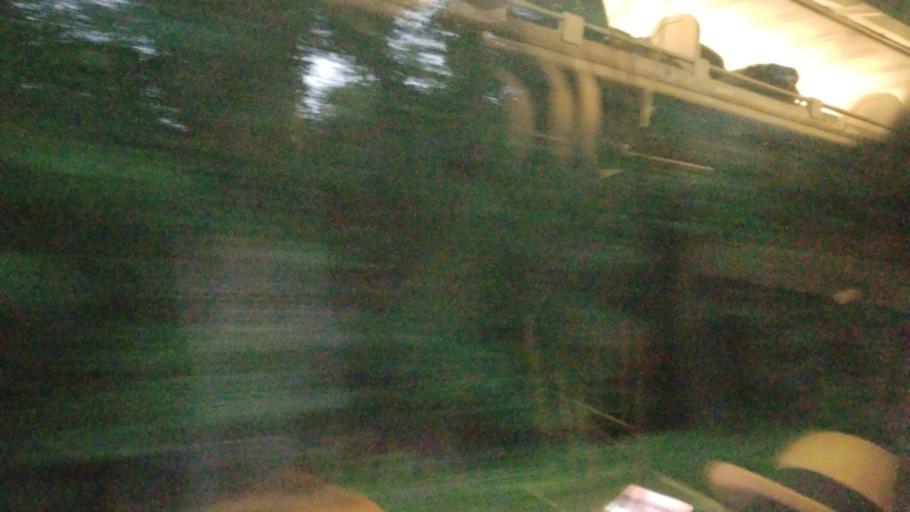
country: US
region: Virginia
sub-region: Orange County
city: Orange
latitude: 38.2263
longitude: -78.1794
